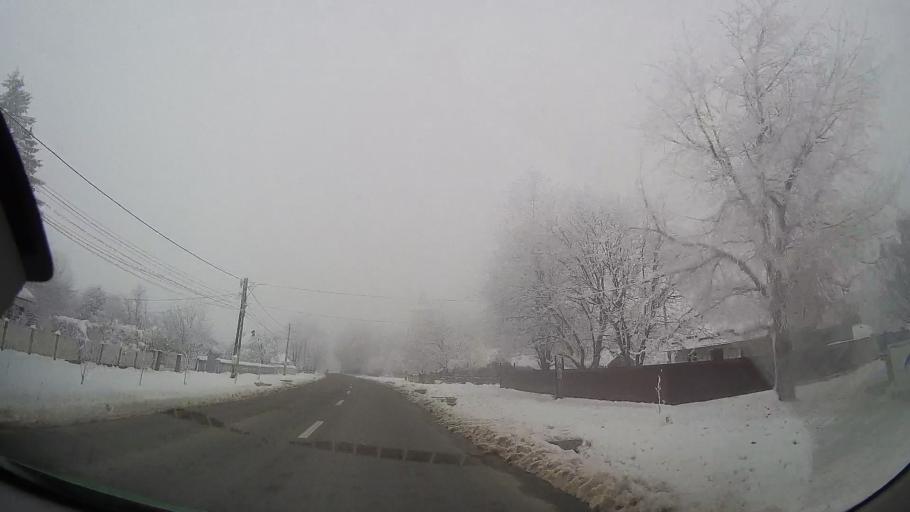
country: RO
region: Iasi
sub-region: Comuna Mogosesti-Siret
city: Mogosesti-Siret
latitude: 47.1644
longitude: 26.7705
